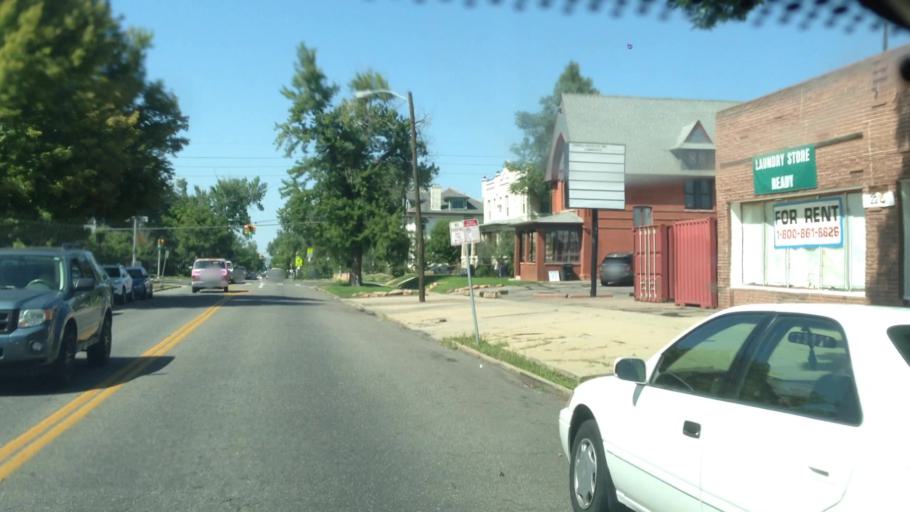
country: US
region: Colorado
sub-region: Denver County
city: Denver
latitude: 39.7499
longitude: -104.9733
